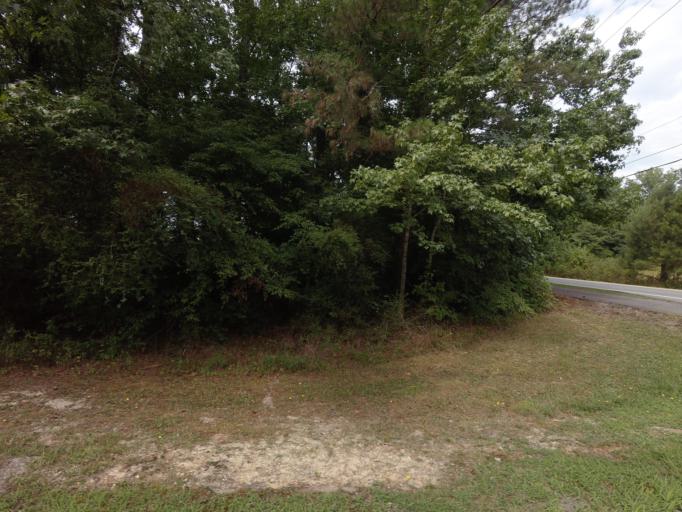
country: US
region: Georgia
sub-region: Gwinnett County
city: Duluth
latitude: 34.0445
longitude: -84.1391
